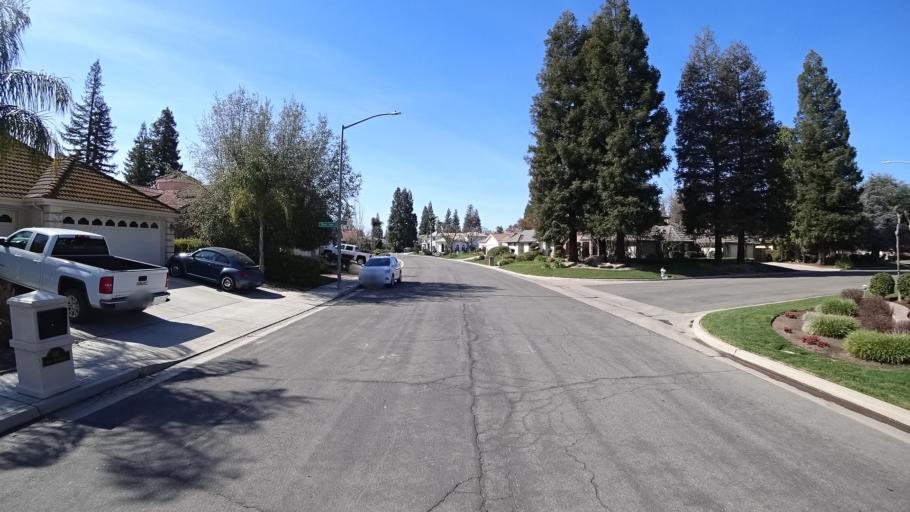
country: US
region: California
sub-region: Fresno County
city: Clovis
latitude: 36.8927
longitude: -119.7682
